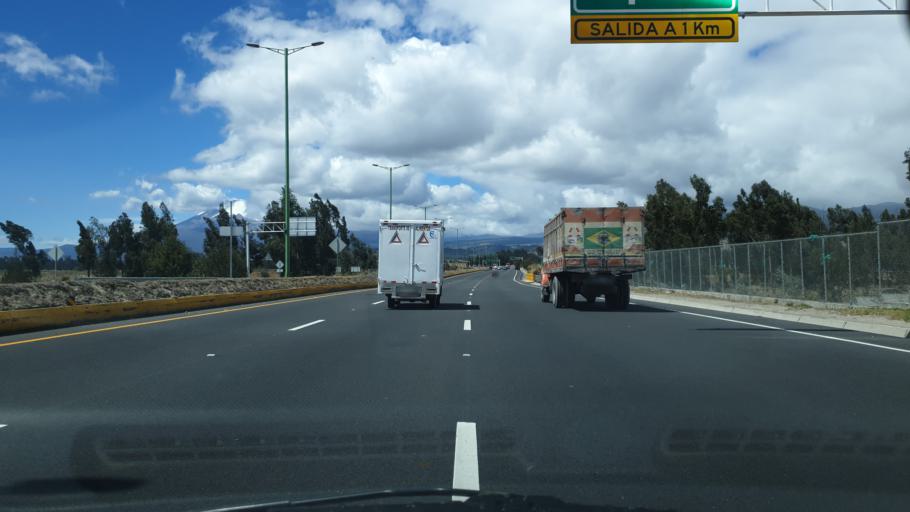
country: EC
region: Cotopaxi
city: Saquisili
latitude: -0.8705
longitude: -78.6362
